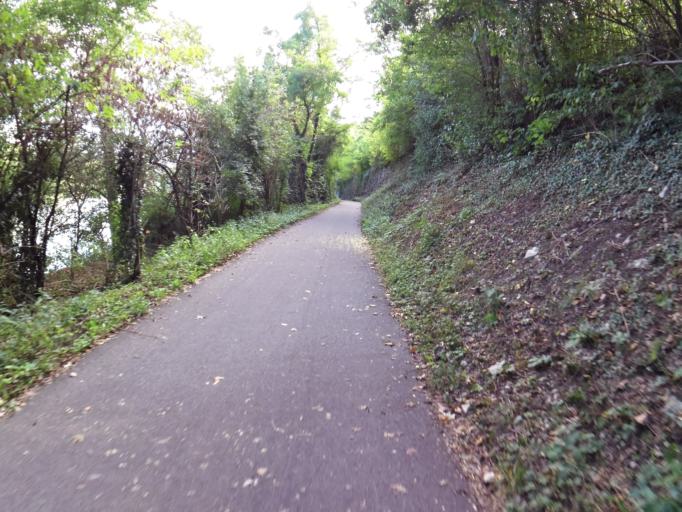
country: DE
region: Baden-Wuerttemberg
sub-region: Regierungsbezirk Stuttgart
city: Gemmrigheim
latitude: 49.0272
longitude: 9.1508
